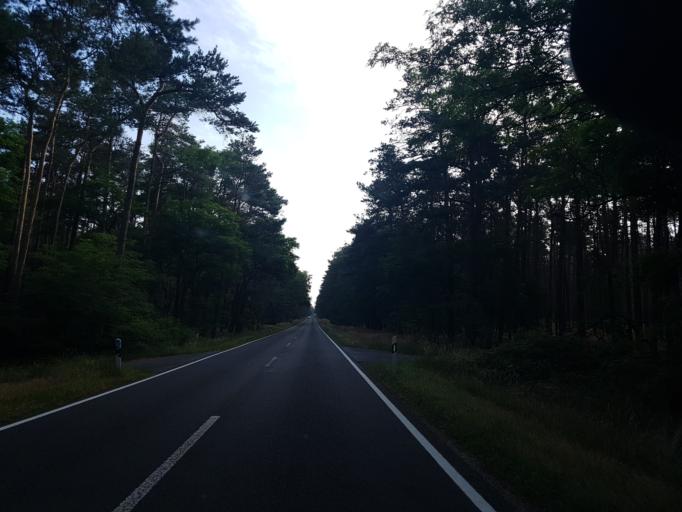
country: DE
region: Brandenburg
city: Schlieben
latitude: 51.7428
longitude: 13.3359
